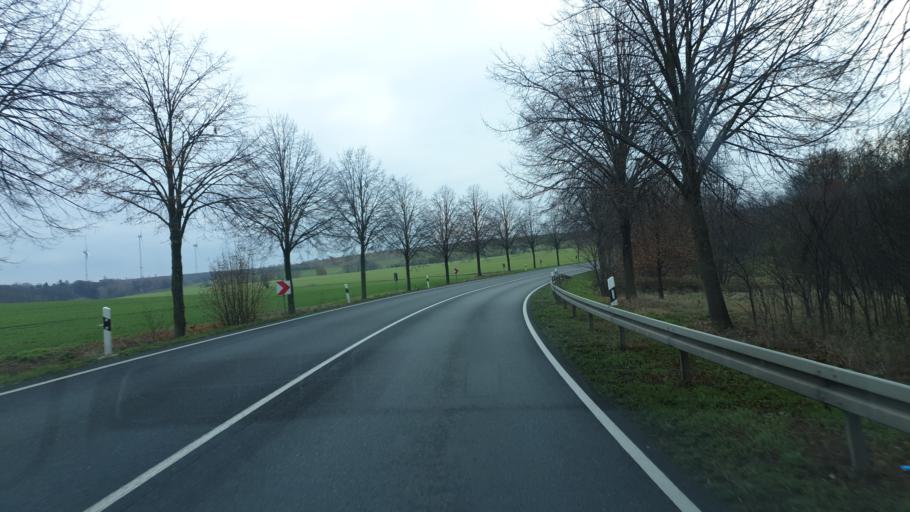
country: DE
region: Saxony-Anhalt
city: Stossen
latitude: 51.1241
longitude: 11.9072
